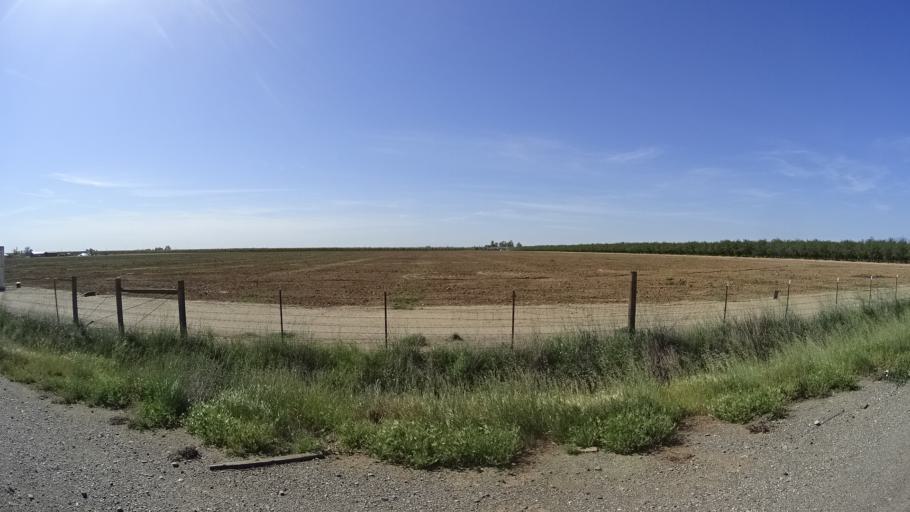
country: US
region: California
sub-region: Glenn County
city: Willows
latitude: 39.6241
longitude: -122.1840
